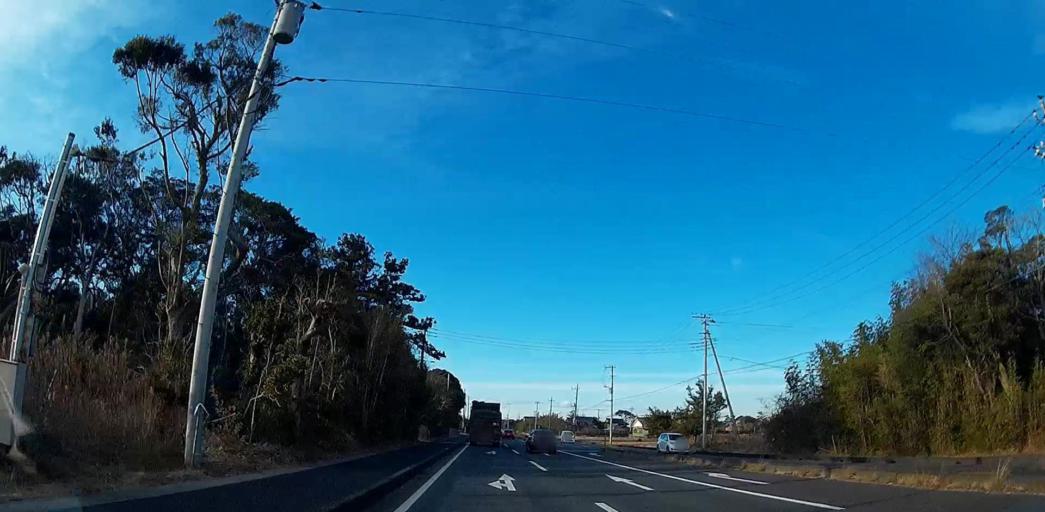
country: JP
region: Chiba
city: Omigawa
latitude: 35.8342
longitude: 140.7184
